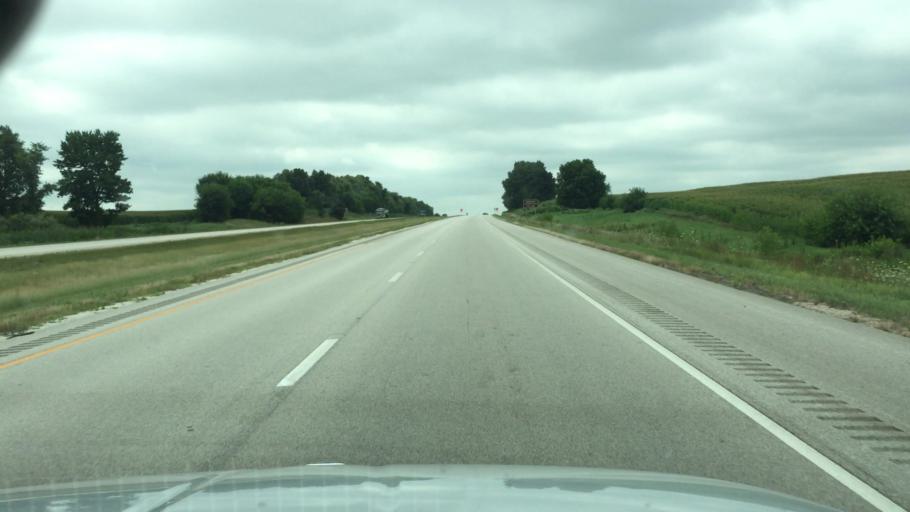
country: US
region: Illinois
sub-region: Henry County
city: Orion
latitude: 41.3117
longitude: -90.3342
